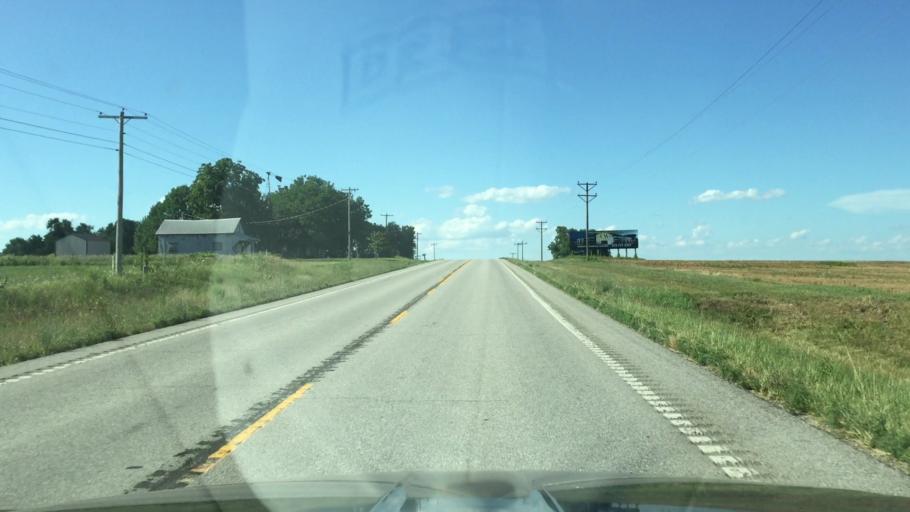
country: US
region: Missouri
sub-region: Morgan County
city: Versailles
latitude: 38.5346
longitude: -92.7981
